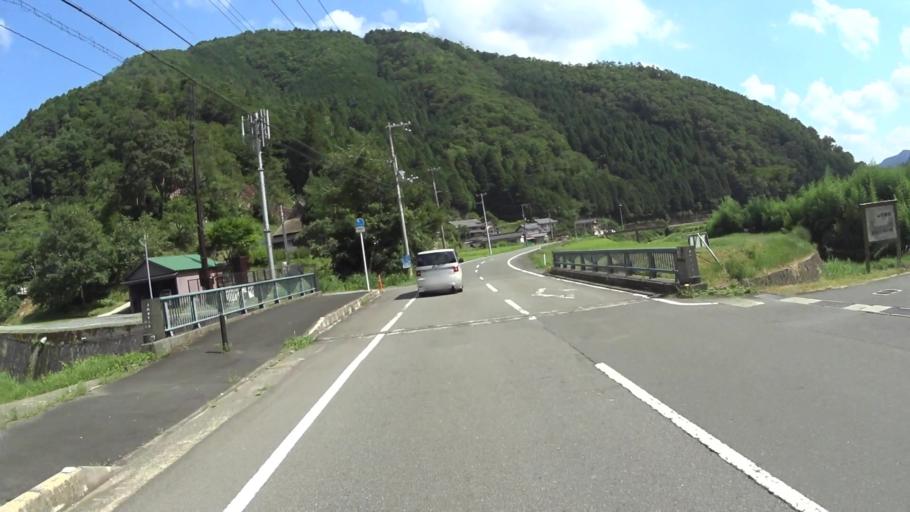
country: JP
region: Kyoto
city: Maizuru
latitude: 35.3041
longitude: 135.5572
